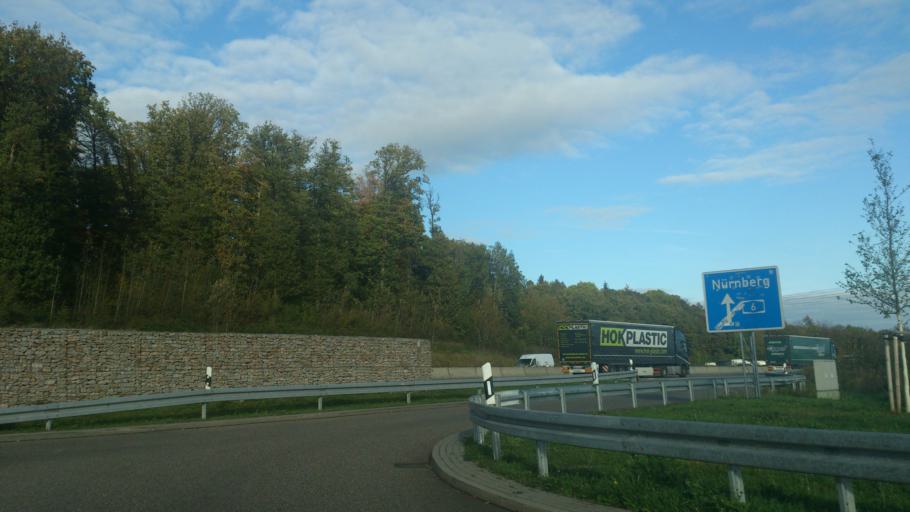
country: DE
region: Baden-Wuerttemberg
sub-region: Regierungsbezirk Stuttgart
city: Kirchardt
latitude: 49.2217
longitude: 8.9722
